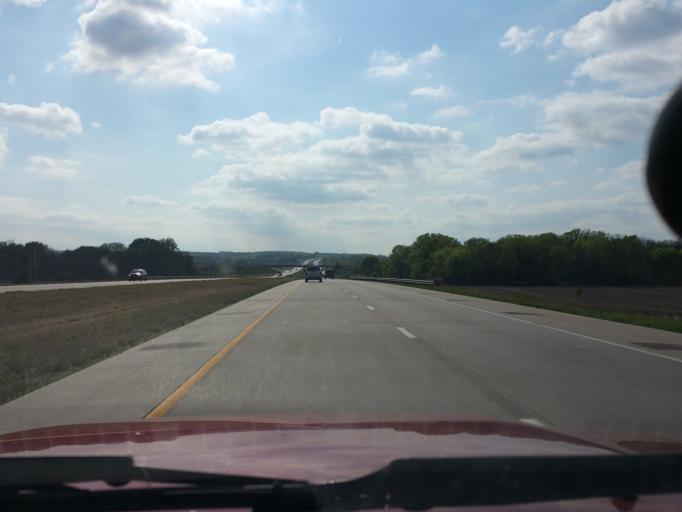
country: US
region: Kansas
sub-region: Wabaunsee County
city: Alma
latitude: 39.0583
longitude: -96.1418
